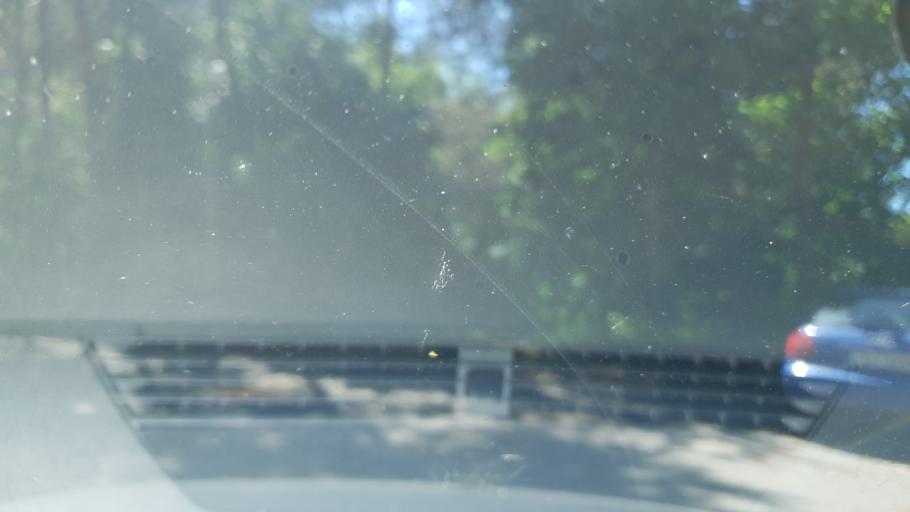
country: PL
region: Pomeranian Voivodeship
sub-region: Gdynia
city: Wielki Kack
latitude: 54.4700
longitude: 18.4783
